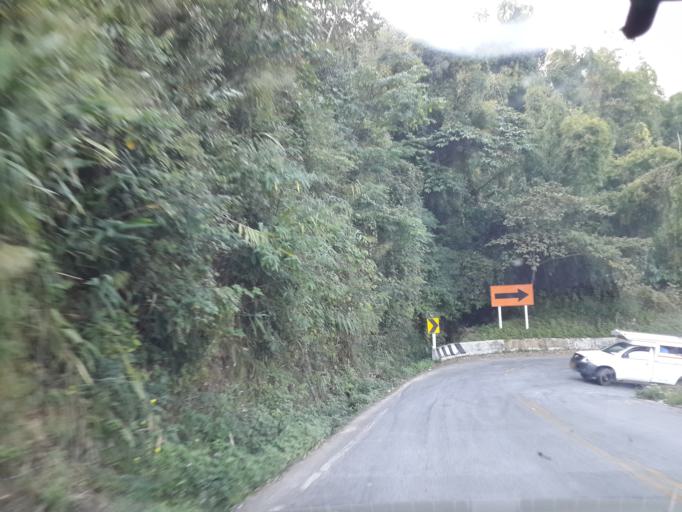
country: TH
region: Chiang Mai
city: Chai Prakan
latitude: 19.8511
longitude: 99.0664
